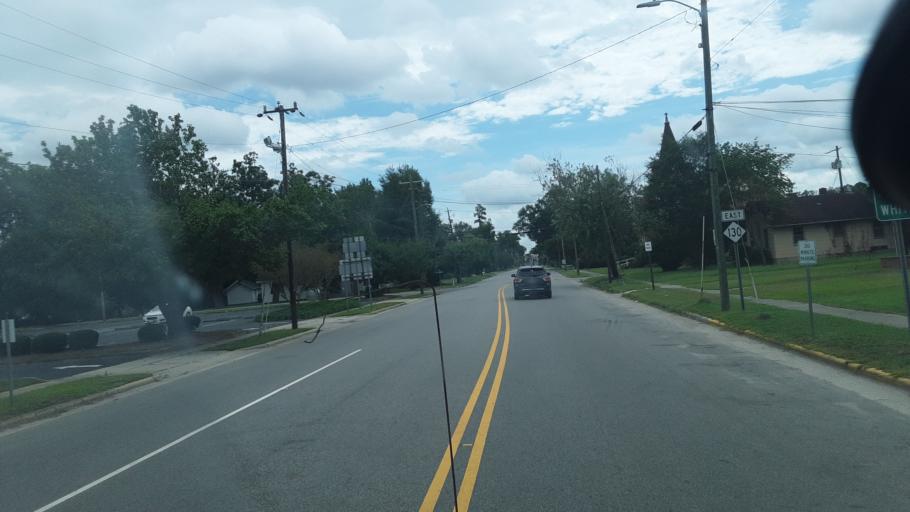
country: US
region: North Carolina
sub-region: Robeson County
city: Rowland
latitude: 34.5365
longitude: -79.2911
